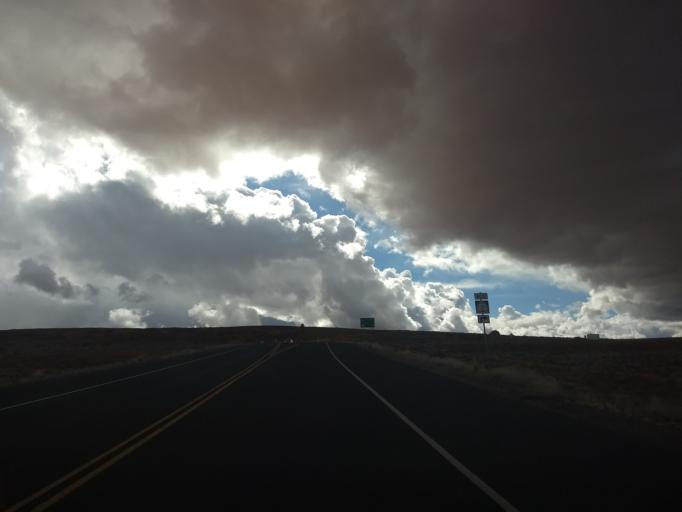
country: US
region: Utah
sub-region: Washington County
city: Washington
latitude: 37.1081
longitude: -113.3956
